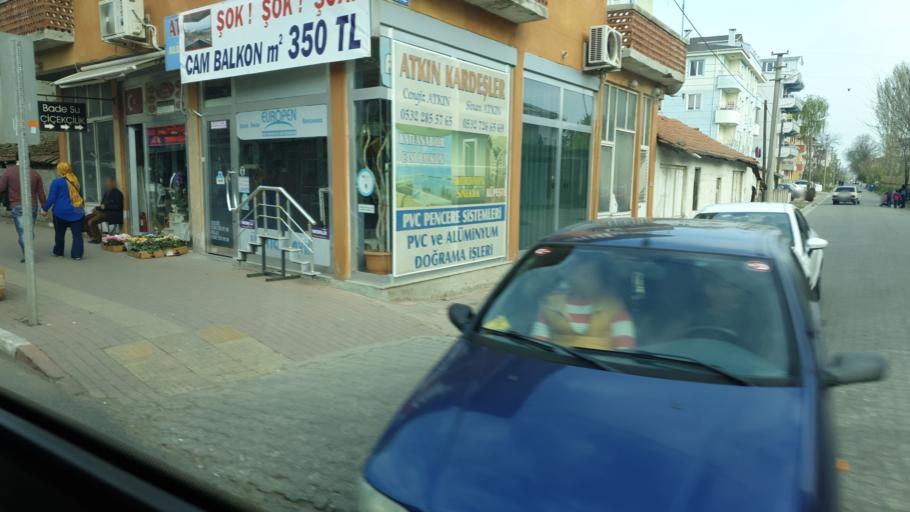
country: TR
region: Tekirdag
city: Muratli
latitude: 41.1732
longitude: 27.4973
